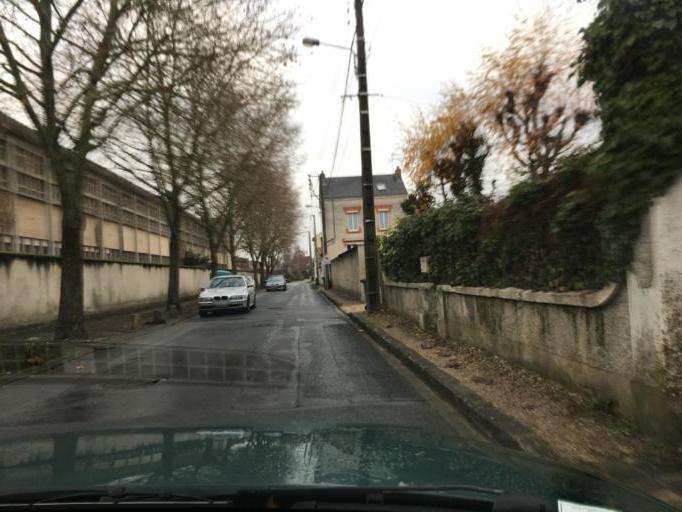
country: FR
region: Centre
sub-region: Departement du Loiret
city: Olivet
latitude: 47.8749
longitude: 1.9082
